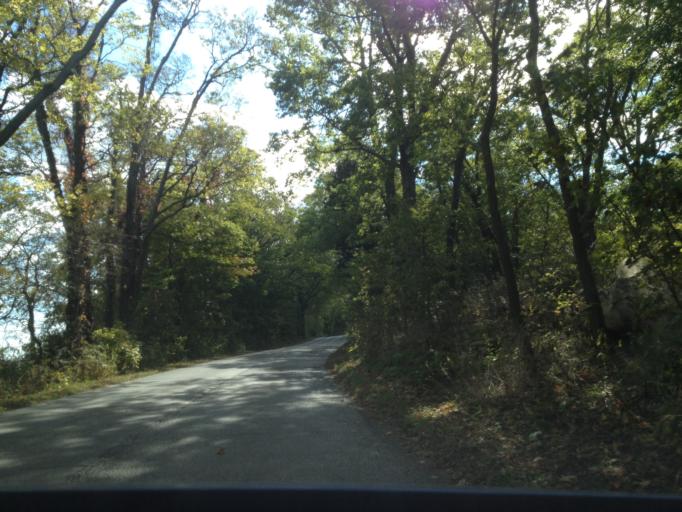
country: CA
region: Ontario
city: Amherstburg
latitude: 41.9847
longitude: -82.5469
